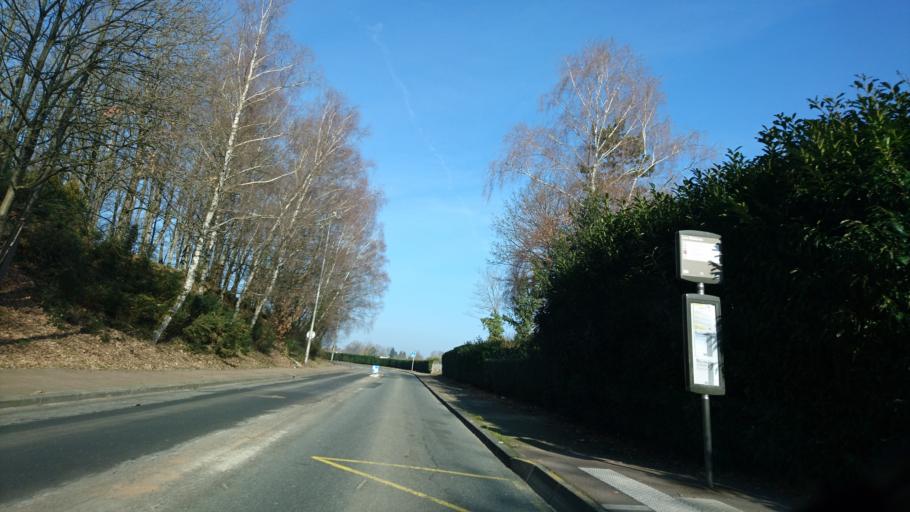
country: FR
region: Limousin
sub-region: Departement de la Haute-Vienne
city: Rilhac-Rancon
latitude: 45.8822
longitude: 1.2989
